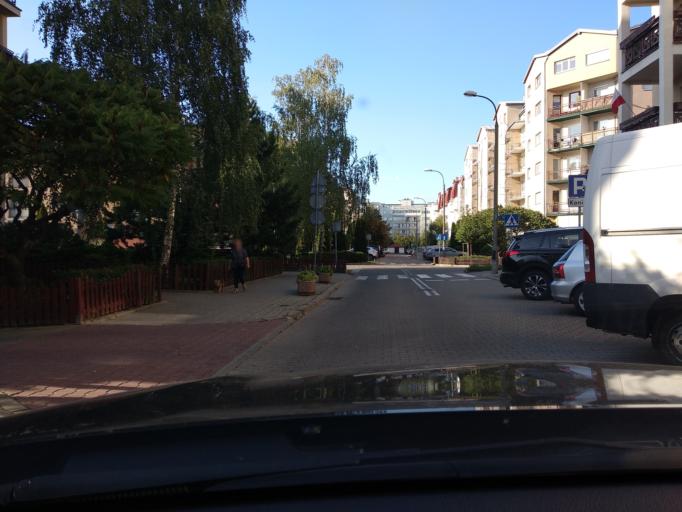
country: PL
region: Masovian Voivodeship
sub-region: Warszawa
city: Kabaty
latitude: 52.1293
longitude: 21.0589
